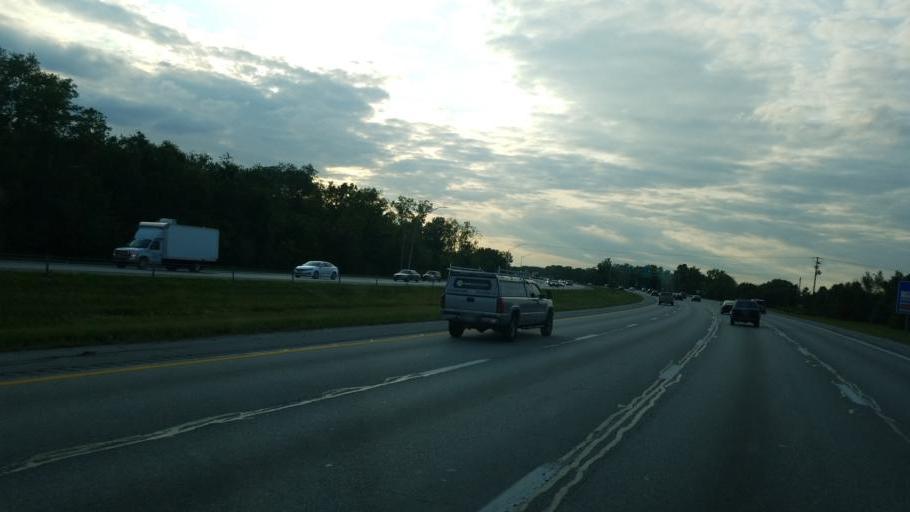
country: US
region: Ohio
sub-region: Franklin County
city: Gahanna
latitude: 40.0016
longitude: -82.8596
